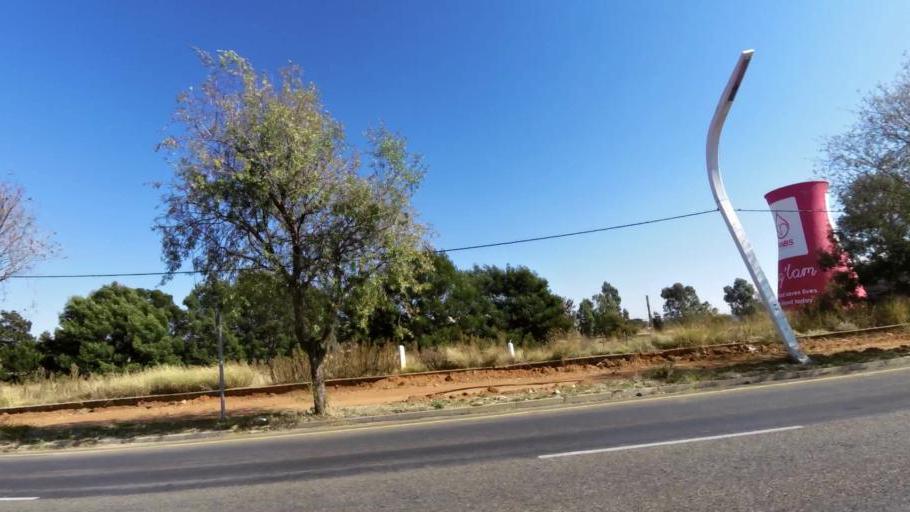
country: ZA
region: Gauteng
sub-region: City of Johannesburg Metropolitan Municipality
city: Johannesburg
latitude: -26.2385
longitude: 27.9855
